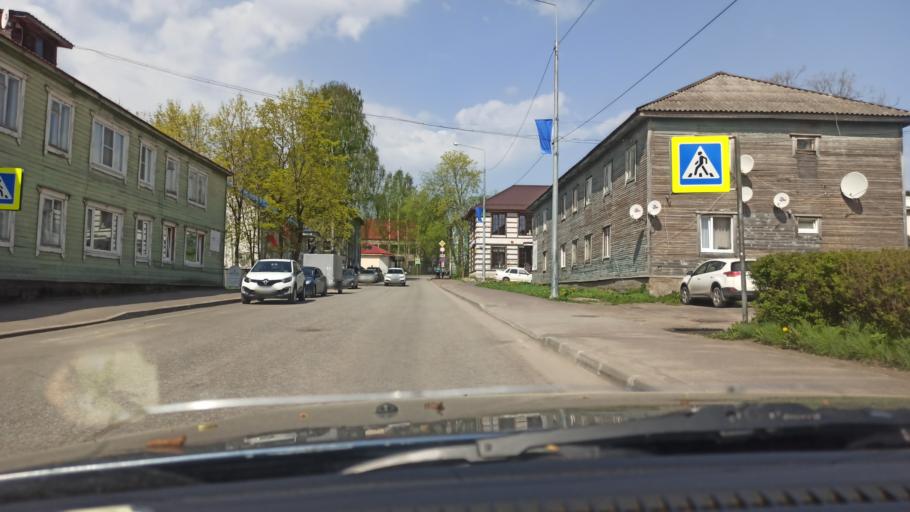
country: RU
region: Republic of Karelia
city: Lakhdenpokh'ya
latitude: 61.5190
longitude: 30.1992
